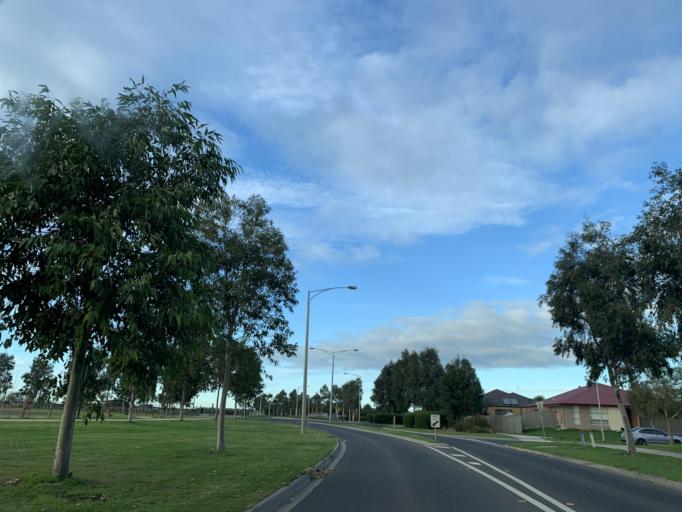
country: AU
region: Victoria
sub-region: Casey
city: Cranbourne East
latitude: -38.1216
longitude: 145.3062
